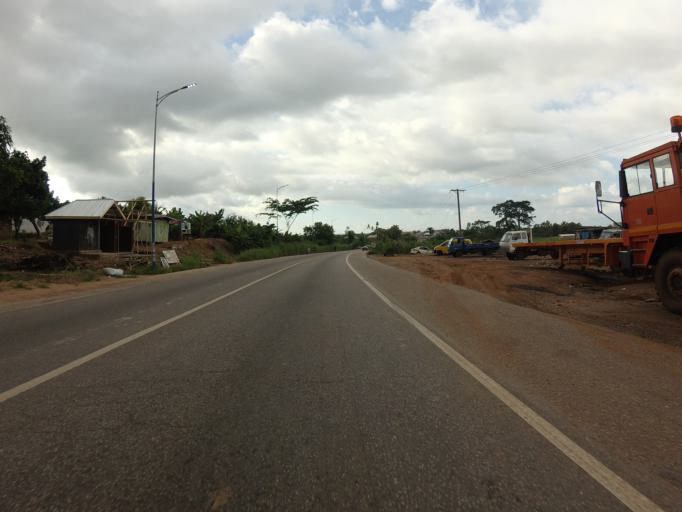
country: GH
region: Ashanti
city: Tafo
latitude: 6.8100
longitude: -1.6489
